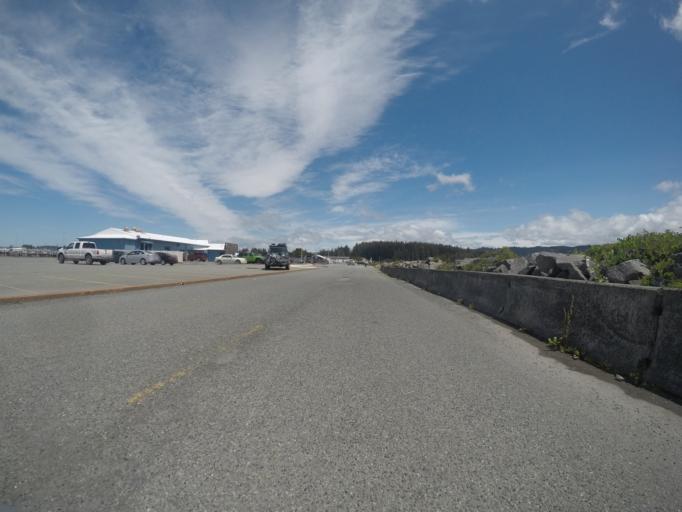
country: US
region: California
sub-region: Del Norte County
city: Bertsch-Oceanview
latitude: 41.7432
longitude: -124.1811
